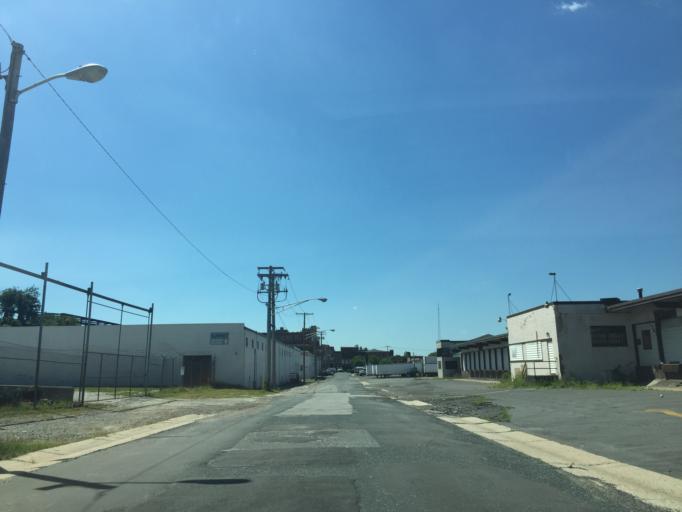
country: US
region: Maryland
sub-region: City of Baltimore
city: Baltimore
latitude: 39.2905
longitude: -76.5598
